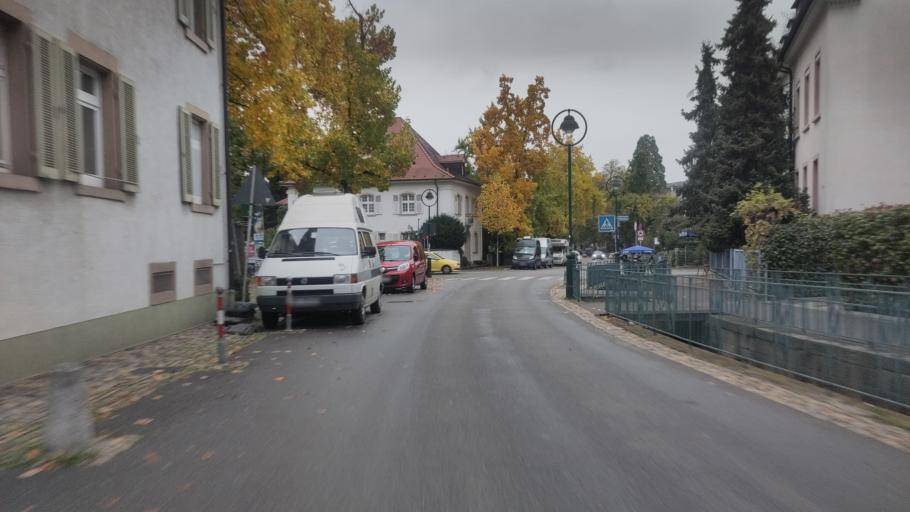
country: DE
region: Baden-Wuerttemberg
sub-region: Freiburg Region
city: Freiburg
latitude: 48.0069
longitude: 7.8620
